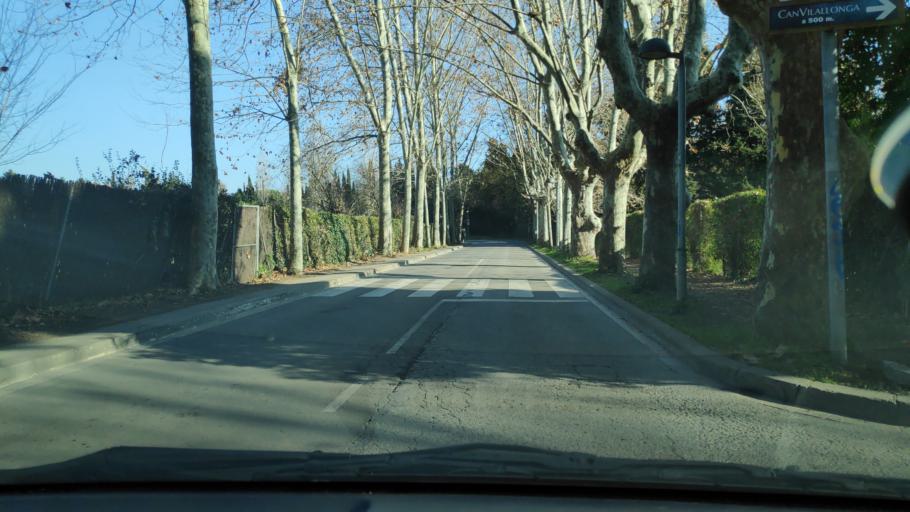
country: ES
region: Catalonia
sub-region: Provincia de Barcelona
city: Sant Cugat del Valles
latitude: 41.4624
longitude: 2.0775
